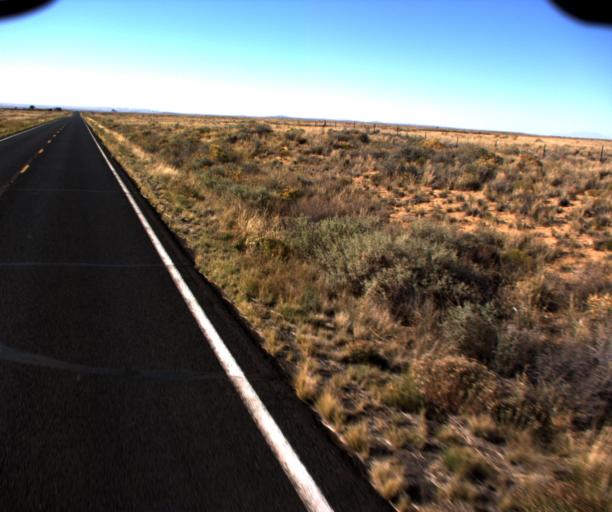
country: US
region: Arizona
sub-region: Navajo County
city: First Mesa
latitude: 35.7830
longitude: -110.5007
